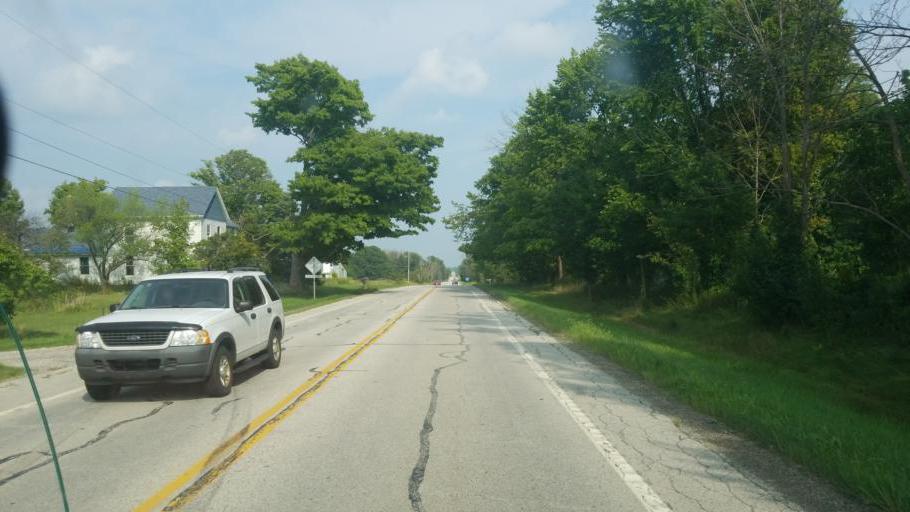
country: US
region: Ohio
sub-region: Medina County
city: Medina
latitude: 41.1676
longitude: -81.9723
